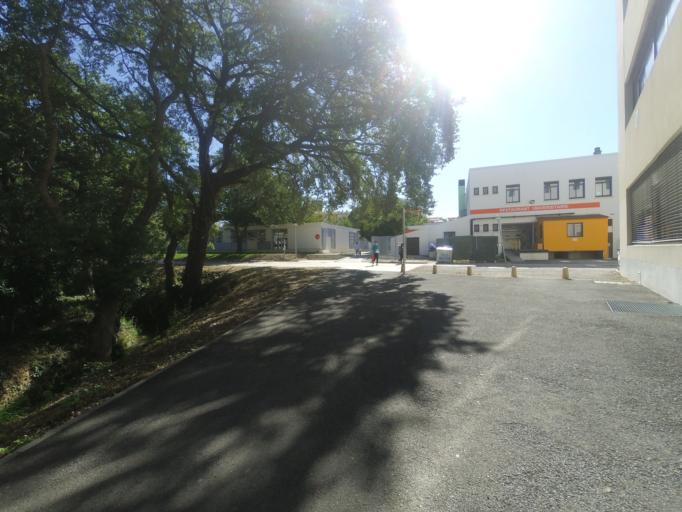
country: FR
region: Languedoc-Roussillon
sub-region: Departement des Pyrenees-Orientales
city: Perpignan
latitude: 42.6820
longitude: 2.9007
